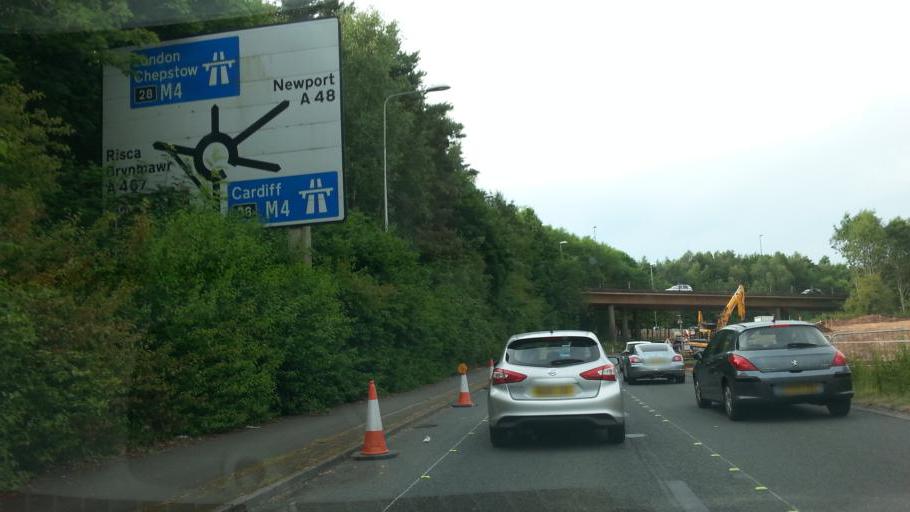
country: GB
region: Wales
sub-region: Newport
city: Newport
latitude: 51.5634
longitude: -3.0356
